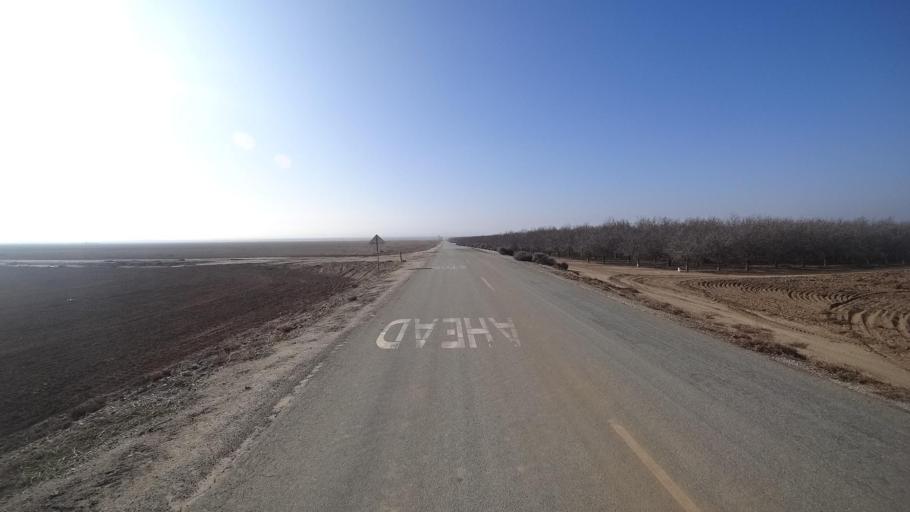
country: US
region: California
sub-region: Kern County
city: Maricopa
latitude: 35.1013
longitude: -119.3407
